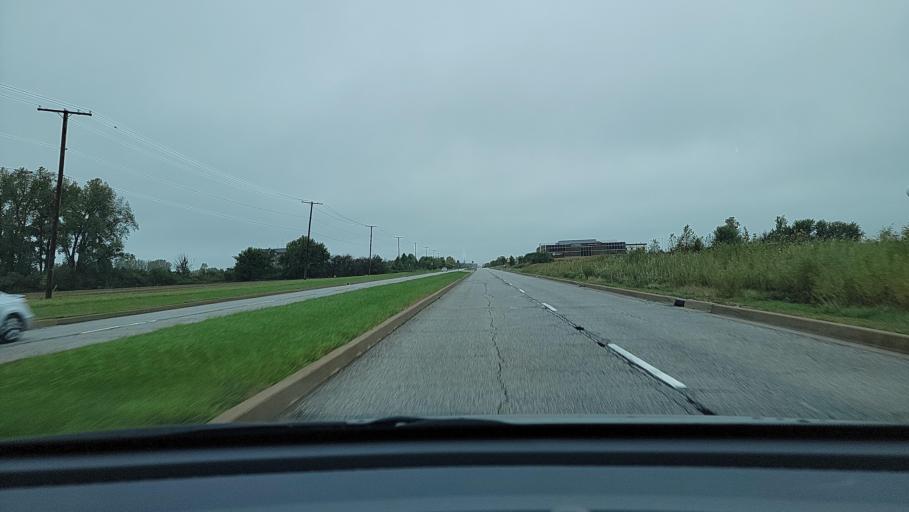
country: US
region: Indiana
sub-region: Porter County
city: Portage
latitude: 41.5418
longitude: -87.1823
